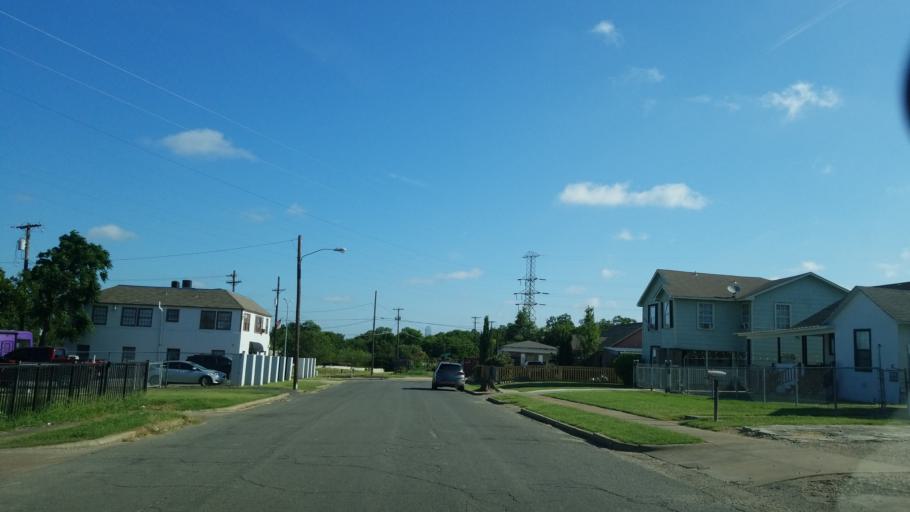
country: US
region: Texas
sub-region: Dallas County
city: Dallas
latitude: 32.7196
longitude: -96.8071
